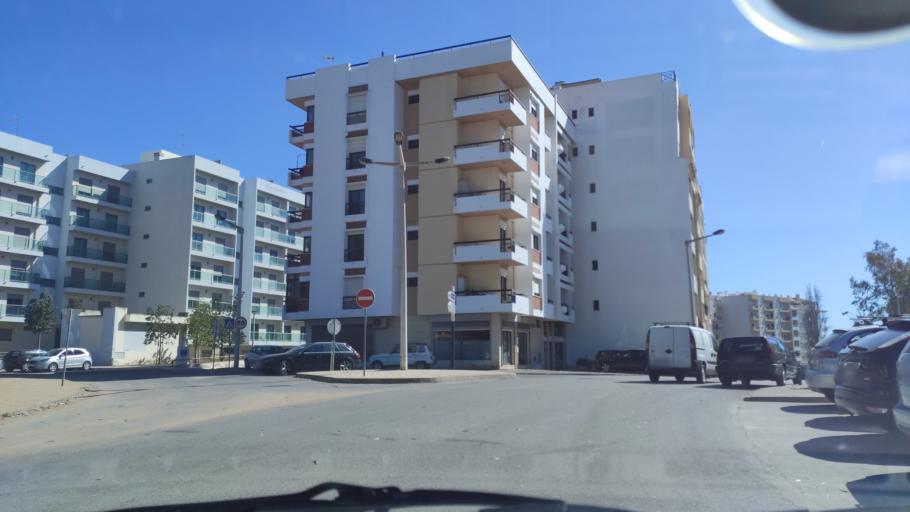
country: PT
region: Faro
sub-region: Faro
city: Faro
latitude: 37.0272
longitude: -7.9356
